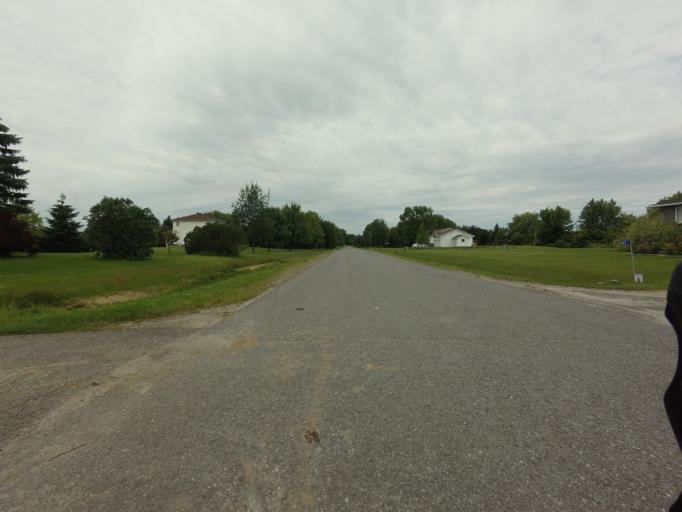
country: CA
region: Ontario
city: Bells Corners
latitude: 45.0238
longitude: -75.6908
